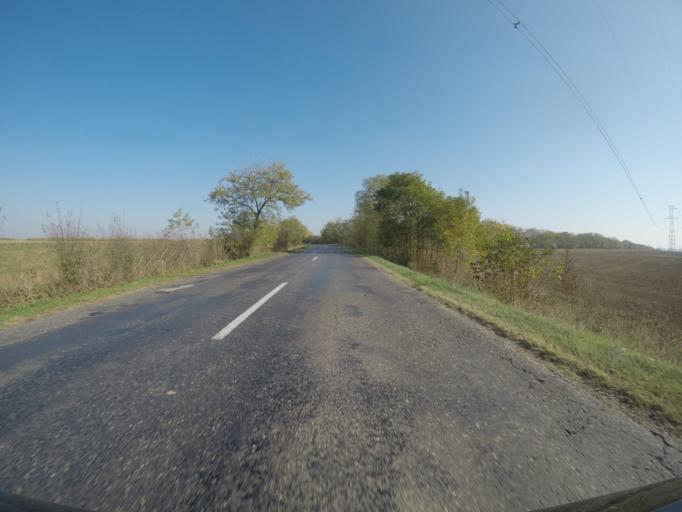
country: HU
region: Tolna
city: Paks
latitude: 46.6002
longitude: 18.7911
